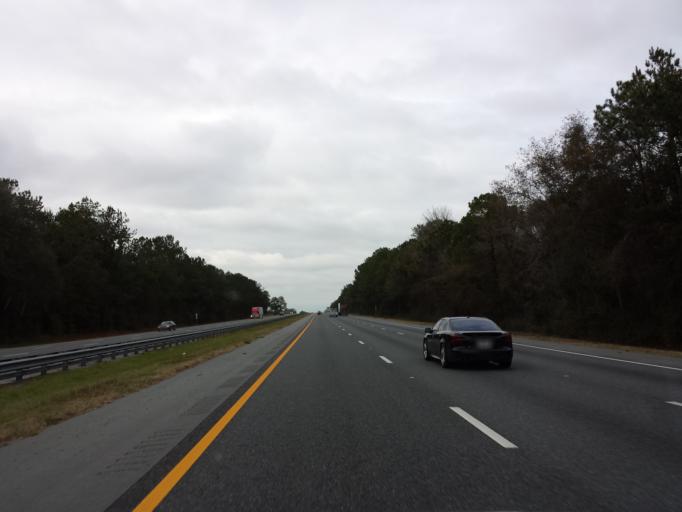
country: US
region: Florida
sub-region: Columbia County
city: Lake City
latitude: 30.0402
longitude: -82.6175
